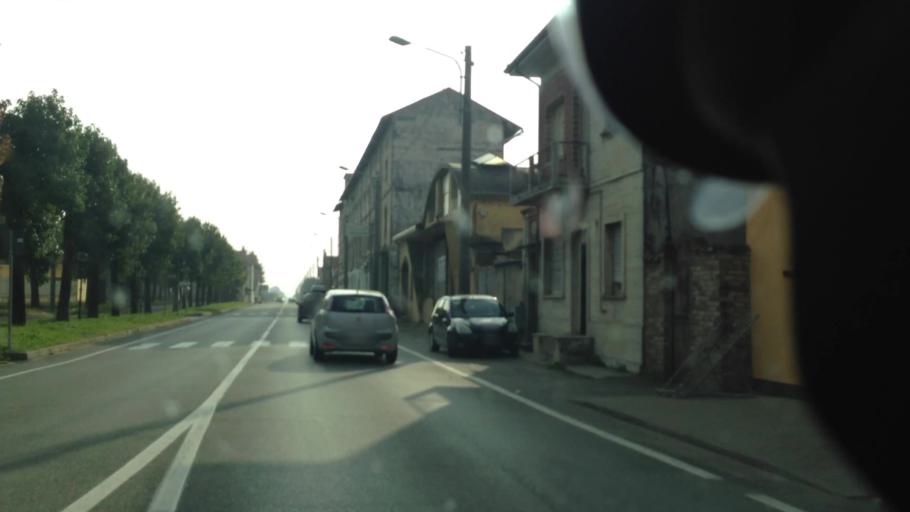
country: IT
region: Piedmont
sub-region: Provincia di Vercelli
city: Borgo d'Ale
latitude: 45.3456
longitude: 8.0499
